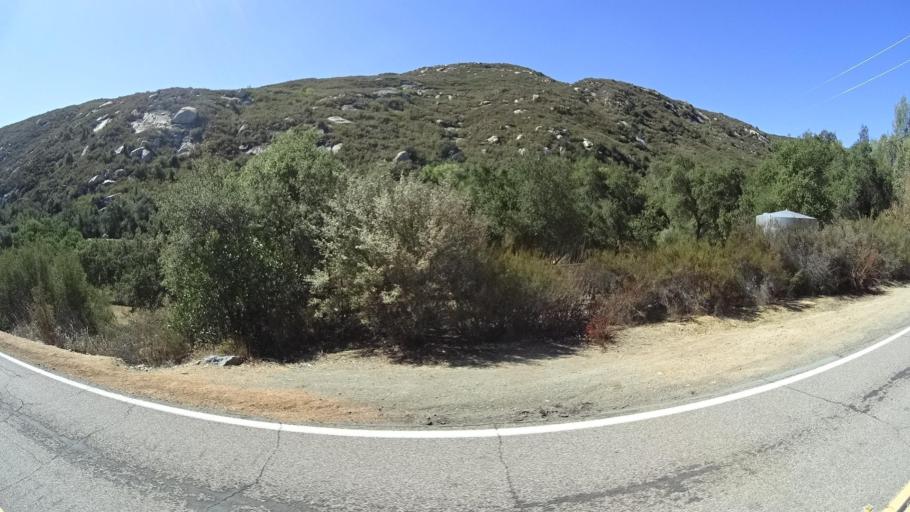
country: US
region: California
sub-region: San Diego County
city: Alpine
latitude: 32.7066
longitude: -116.7343
